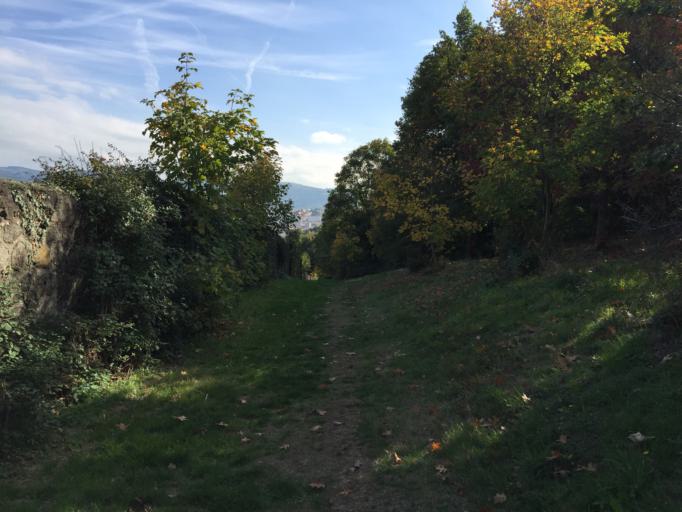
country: FR
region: Rhone-Alpes
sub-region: Departement de la Loire
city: Saint-Priest-en-Jarez
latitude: 45.4527
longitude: 4.3757
